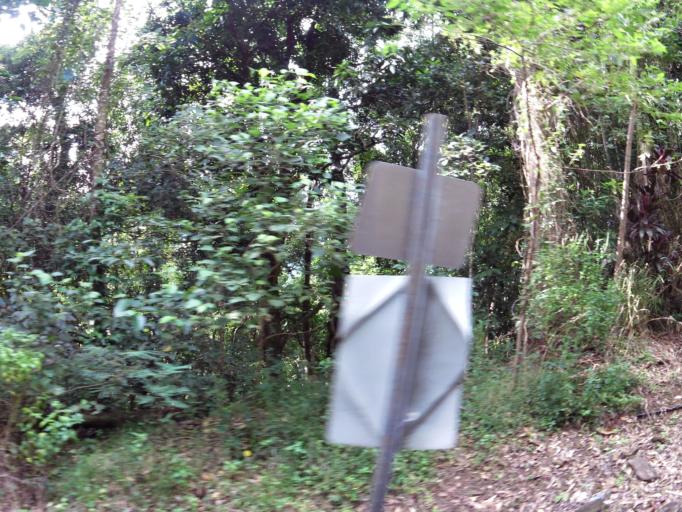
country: AU
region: Queensland
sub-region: Cairns
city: Redlynch
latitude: -16.8795
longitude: 145.6550
